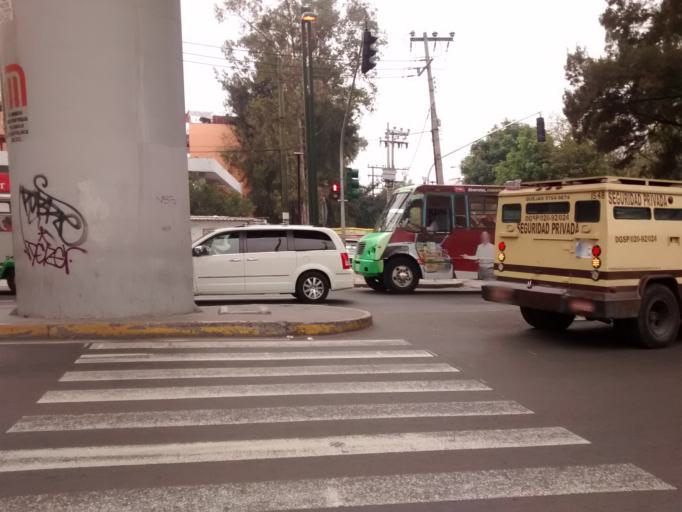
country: MX
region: Mexico City
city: Iztapalapa
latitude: 19.3208
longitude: -99.0872
